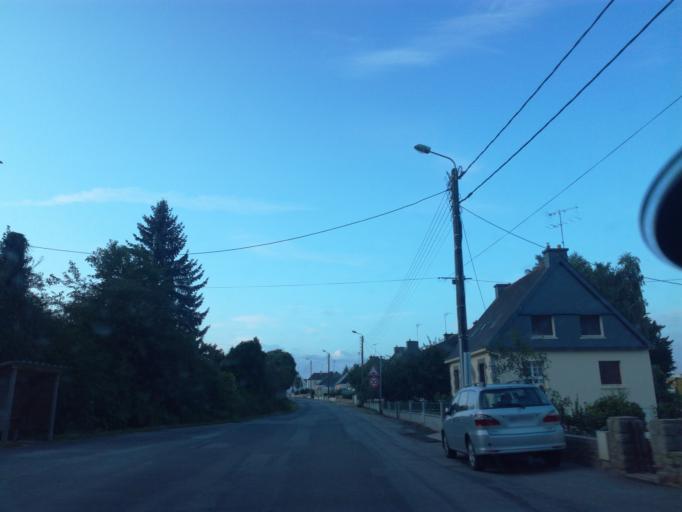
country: FR
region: Brittany
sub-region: Departement du Morbihan
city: Le Sourn
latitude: 48.0439
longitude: -2.9673
